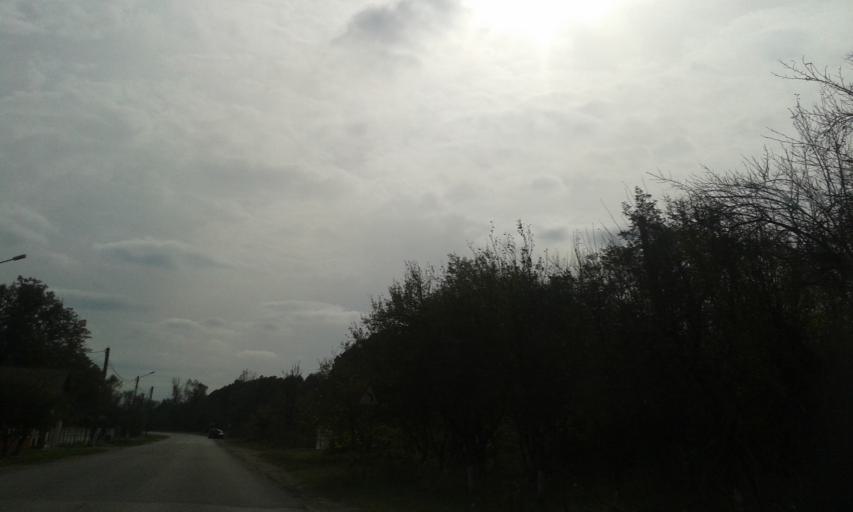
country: RO
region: Gorj
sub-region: Comuna Targu Carbunesti
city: Targu Carbunesti
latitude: 44.9695
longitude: 23.5031
